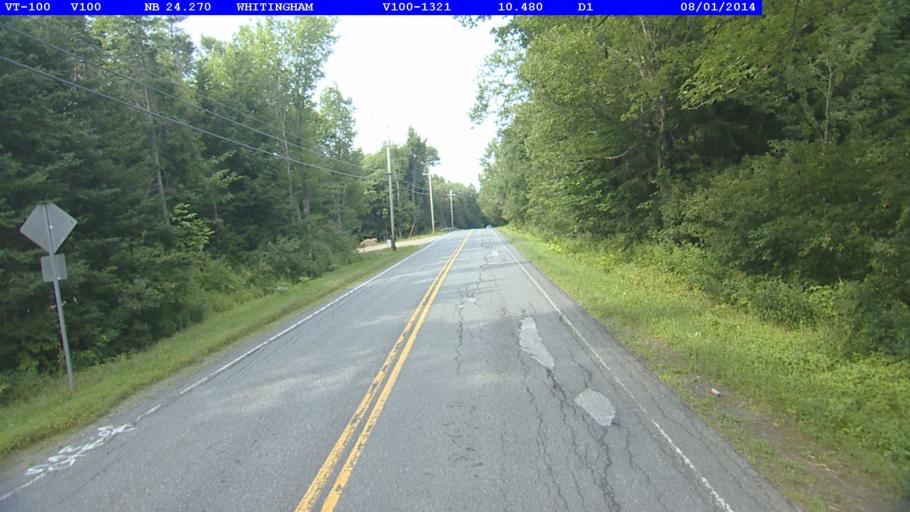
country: US
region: Vermont
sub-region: Windham County
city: Dover
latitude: 42.8250
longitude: -72.8585
